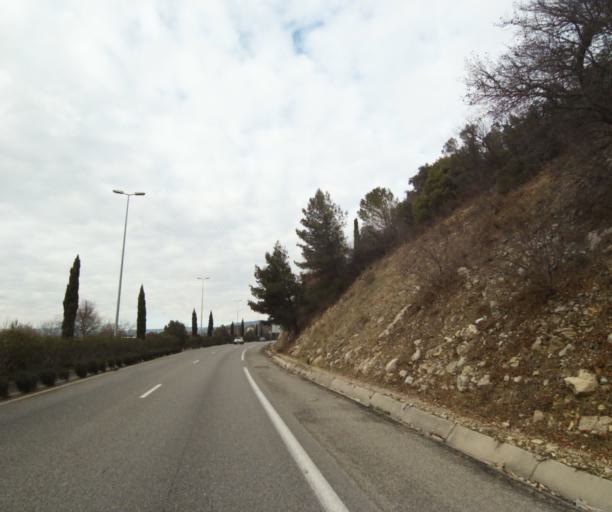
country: FR
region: Provence-Alpes-Cote d'Azur
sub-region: Departement du Var
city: Draguignan
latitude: 43.5178
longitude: 6.4734
